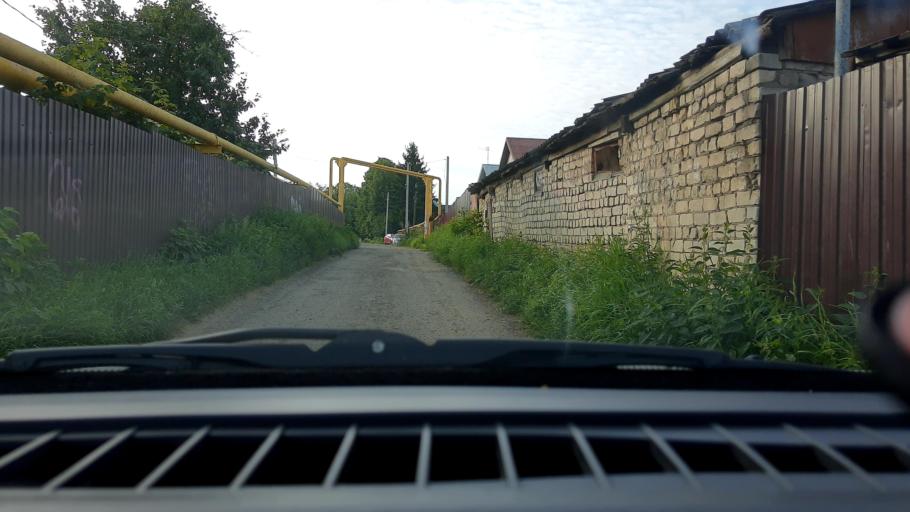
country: RU
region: Nizjnij Novgorod
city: Gorbatovka
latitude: 56.3772
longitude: 43.8258
